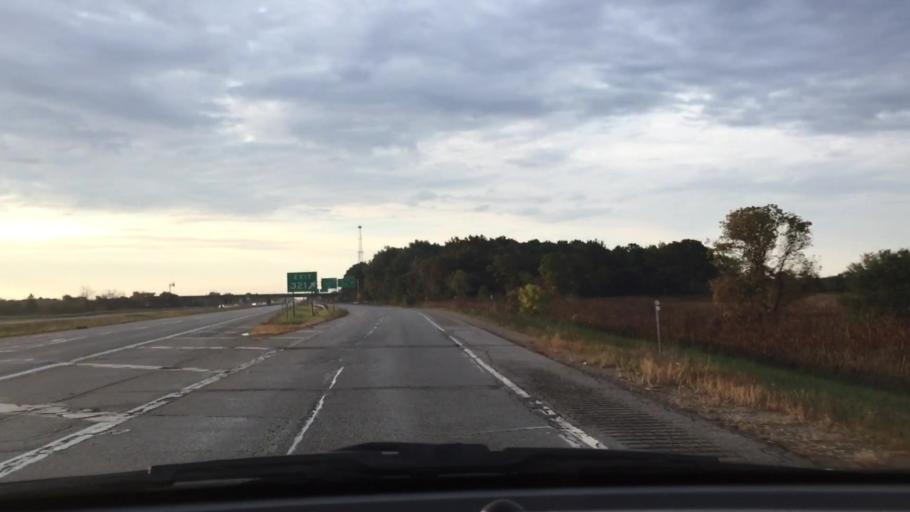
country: US
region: Wisconsin
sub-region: Walworth County
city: Elkhorn
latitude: 42.6794
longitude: -88.5247
